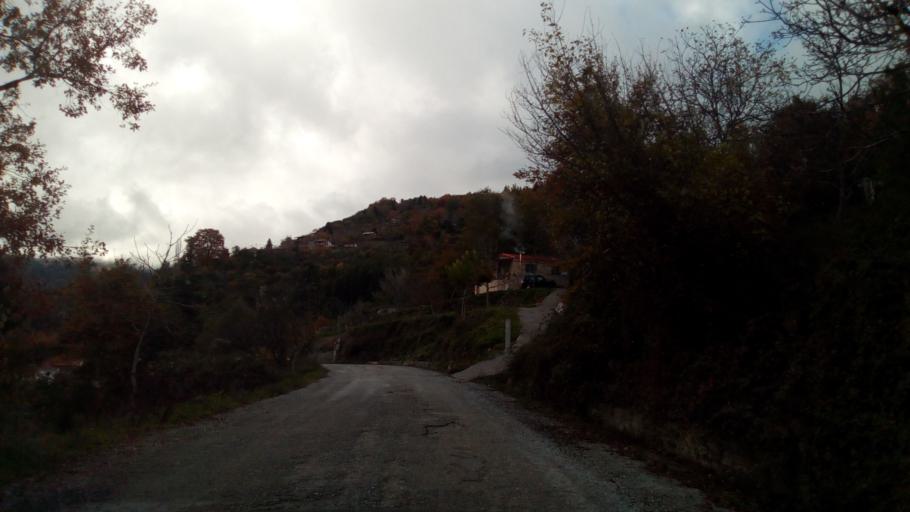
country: GR
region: Central Greece
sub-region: Nomos Fokidos
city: Lidoriki
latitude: 38.5660
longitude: 21.9789
